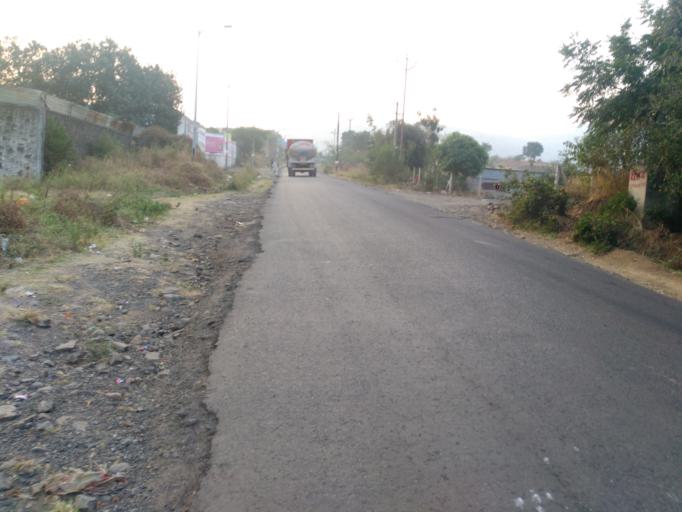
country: IN
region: Maharashtra
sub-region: Pune Division
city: Pune
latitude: 18.4270
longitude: 73.9009
